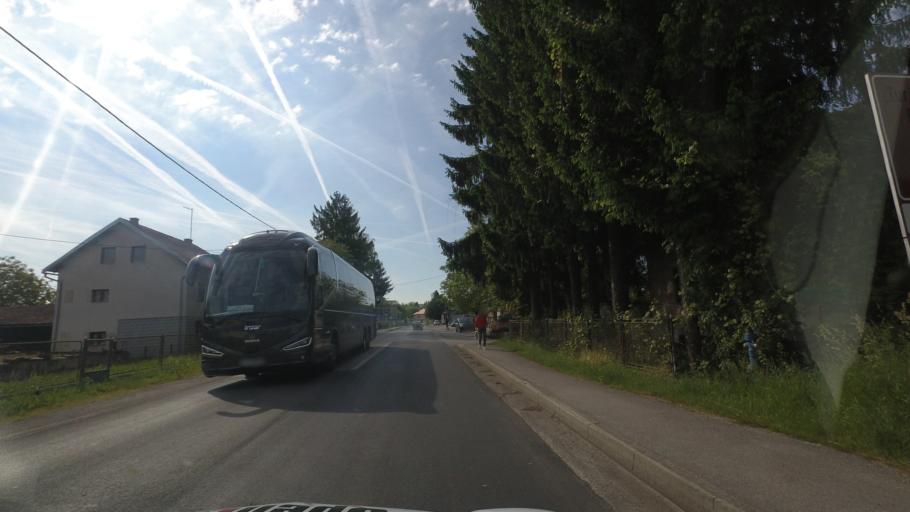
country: HR
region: Karlovacka
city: Vojnic
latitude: 45.3276
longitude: 15.6937
